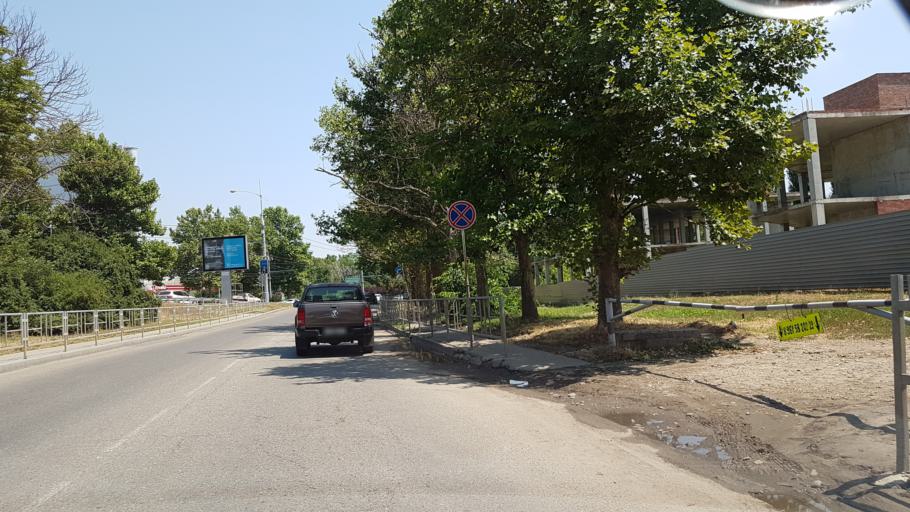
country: RU
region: Krasnodarskiy
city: Pashkovskiy
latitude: 45.0318
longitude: 39.1331
